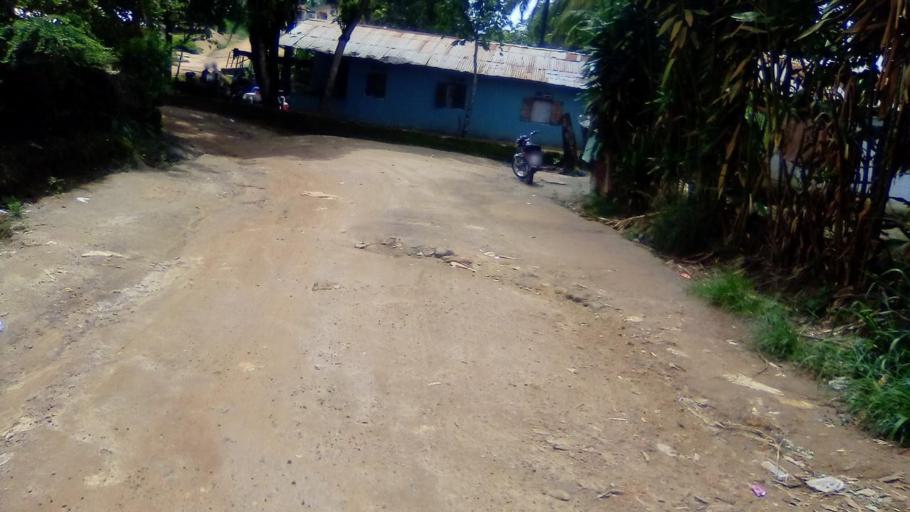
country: SL
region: Southern Province
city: Bo
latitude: 7.9386
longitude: -11.7338
